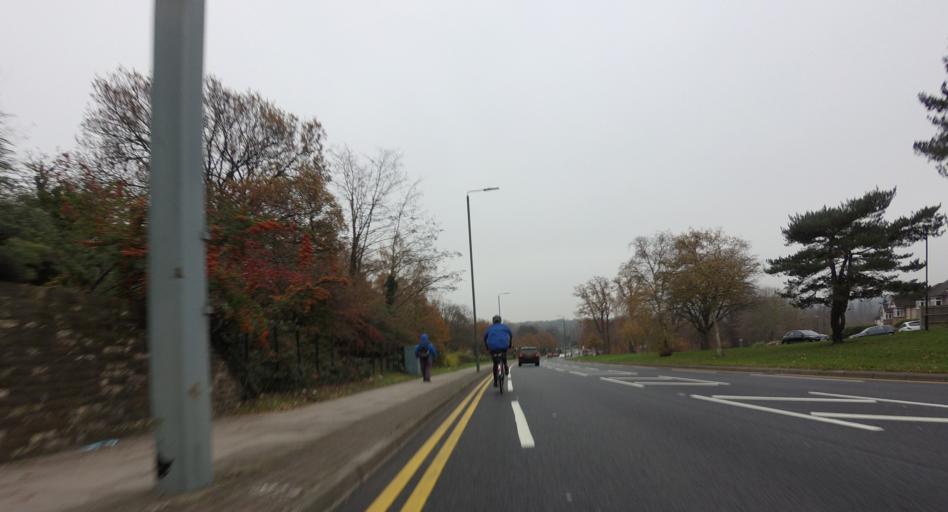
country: GB
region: England
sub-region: Greater London
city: Bexley
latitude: 51.4503
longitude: 0.1556
